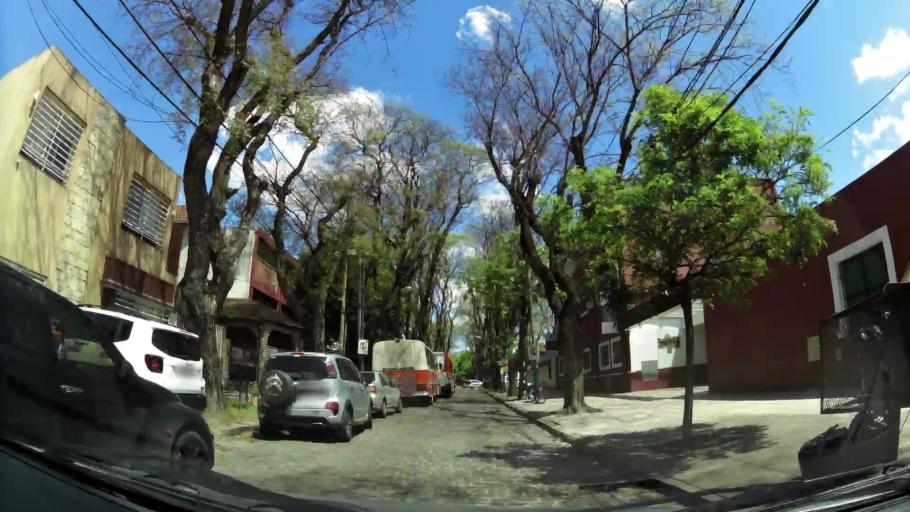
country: AR
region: Buenos Aires
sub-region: Partido de Lomas de Zamora
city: Lomas de Zamora
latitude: -34.7416
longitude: -58.4002
